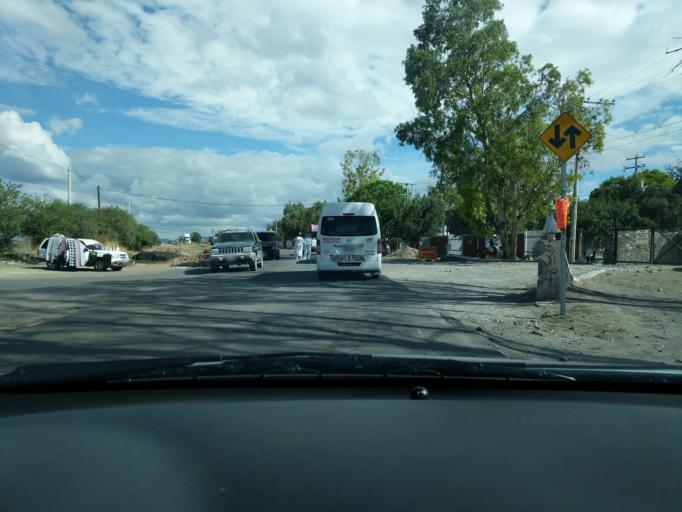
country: MX
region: Queretaro
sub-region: El Marques
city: Hacienda la Cruz [Fraccionamiento]
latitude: 20.6196
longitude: -100.2605
